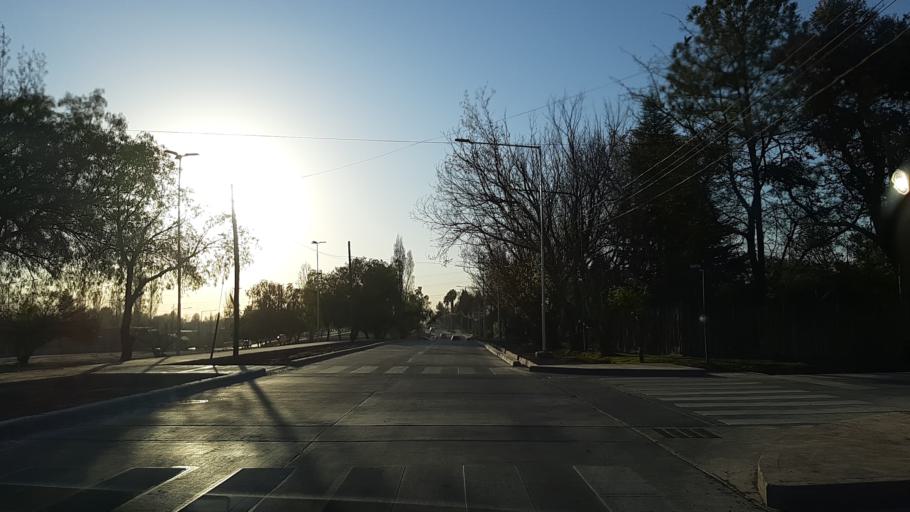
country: AR
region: Mendoza
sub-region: Departamento de Godoy Cruz
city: Godoy Cruz
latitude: -32.9651
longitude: -68.8585
